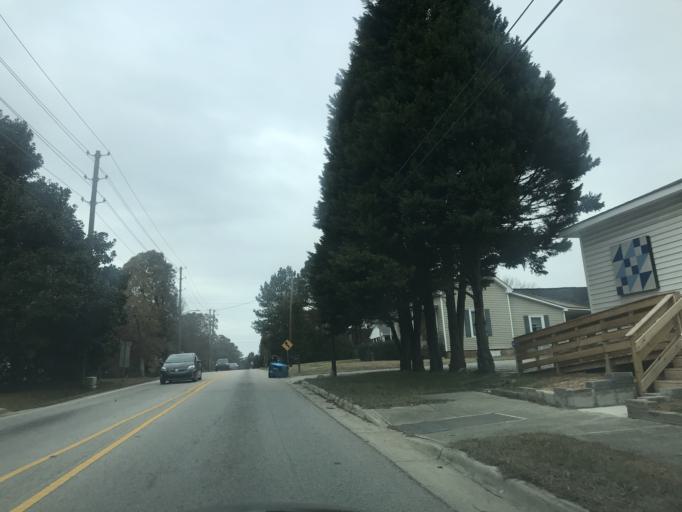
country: US
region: North Carolina
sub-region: Franklin County
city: Youngsville
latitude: 36.0262
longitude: -78.4795
